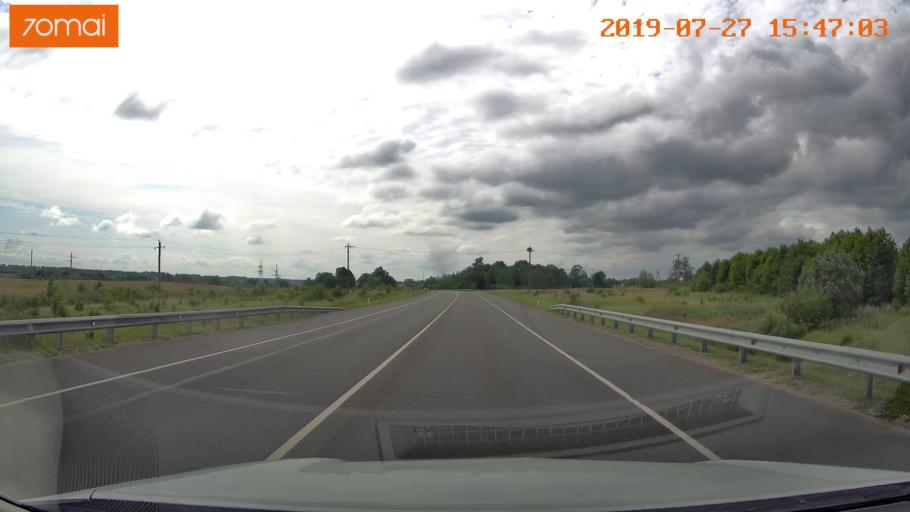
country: RU
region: Kaliningrad
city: Gusev
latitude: 54.6033
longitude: 22.0979
